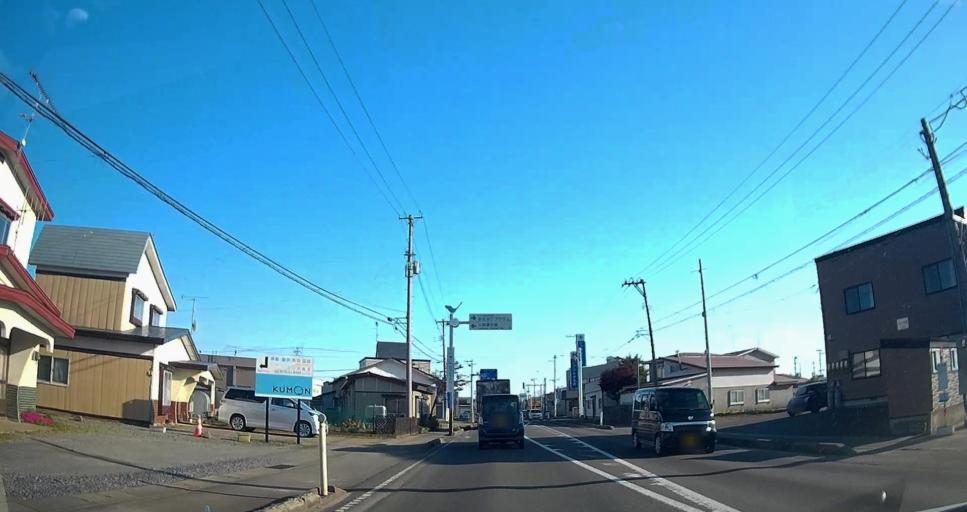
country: JP
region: Aomori
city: Mutsu
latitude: 41.2980
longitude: 141.2215
